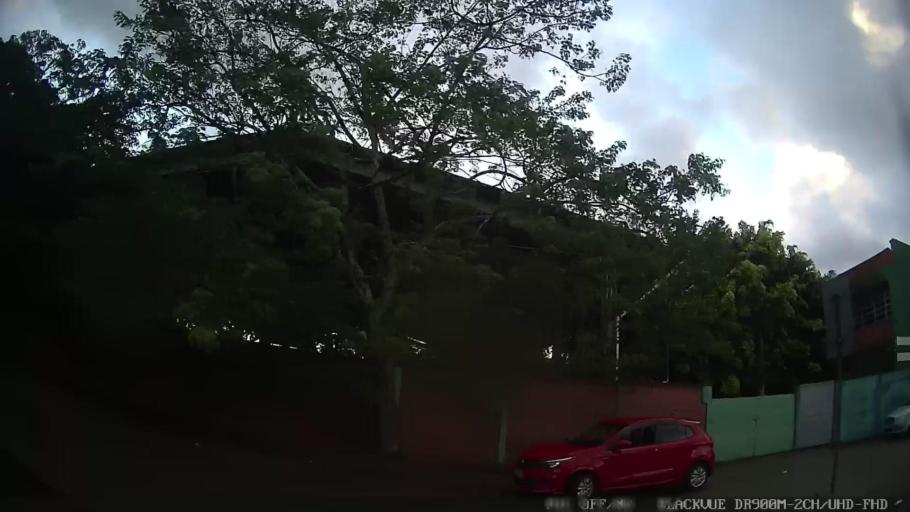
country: BR
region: Sao Paulo
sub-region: Itanhaem
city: Itanhaem
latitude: -24.1695
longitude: -46.7853
